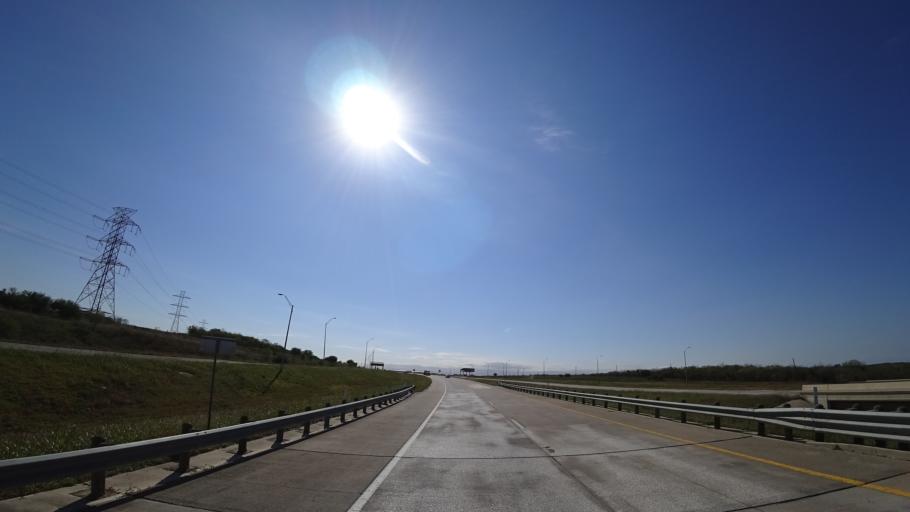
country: US
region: Texas
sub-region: Travis County
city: Onion Creek
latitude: 30.1375
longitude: -97.6656
